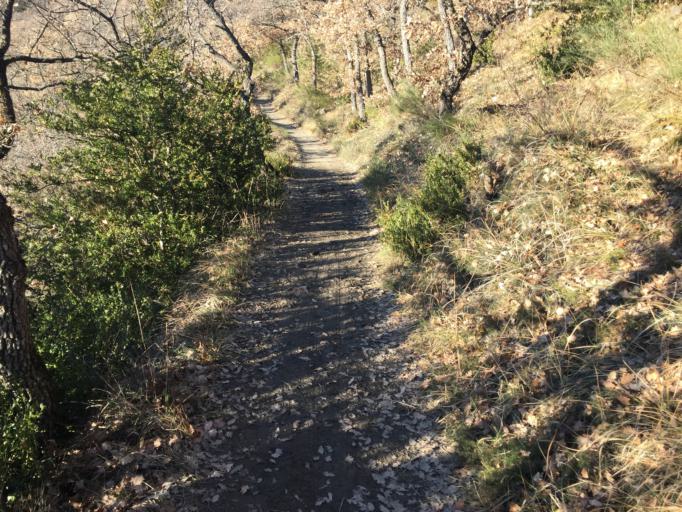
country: FR
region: Provence-Alpes-Cote d'Azur
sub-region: Departement des Alpes-de-Haute-Provence
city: Digne-les-Bains
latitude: 44.0824
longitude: 6.2629
